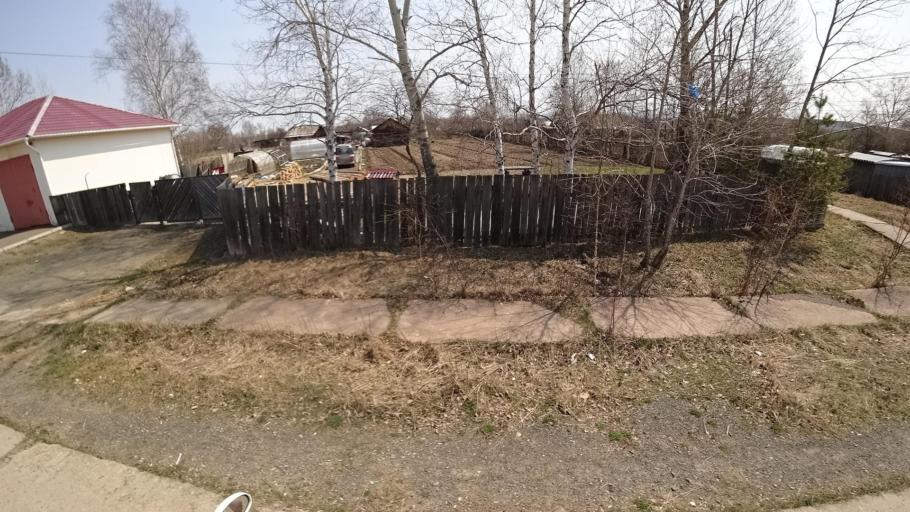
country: RU
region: Khabarovsk Krai
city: Selikhino
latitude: 50.3880
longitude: 137.3735
